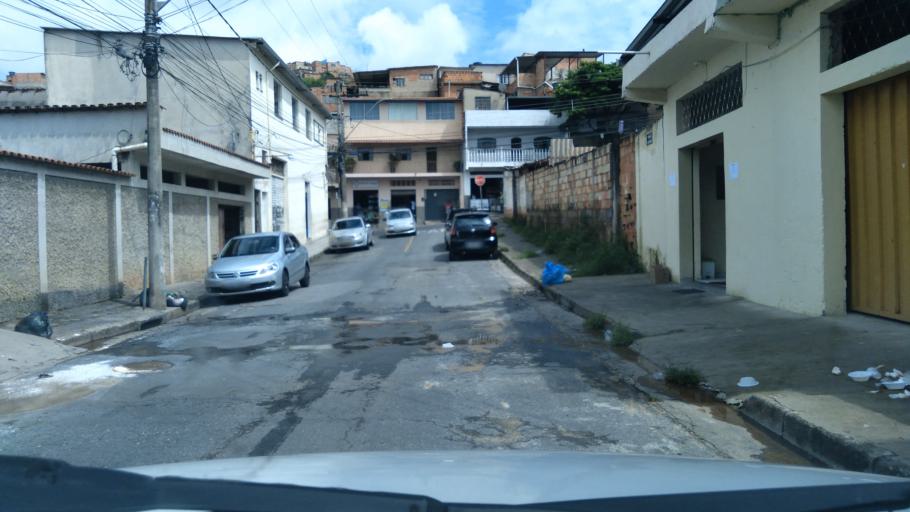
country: BR
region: Minas Gerais
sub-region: Belo Horizonte
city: Belo Horizonte
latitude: -19.8978
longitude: -43.8900
